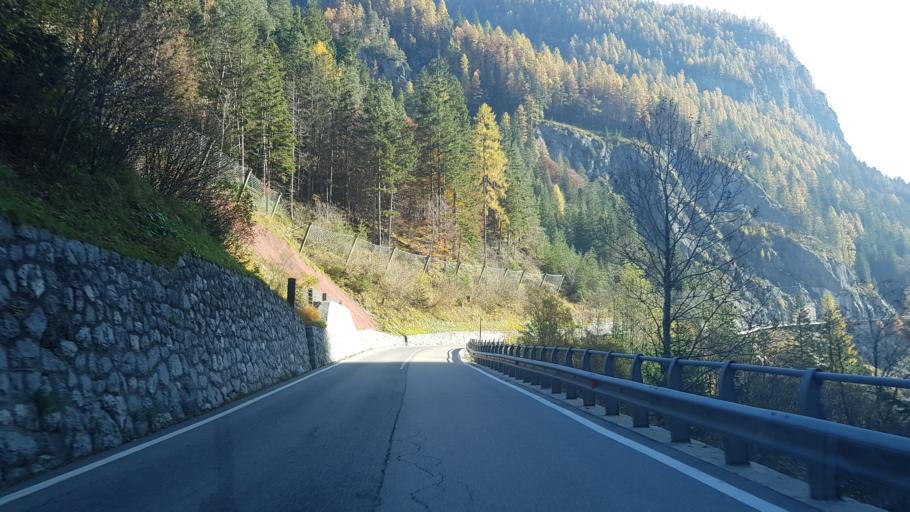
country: IT
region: Veneto
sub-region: Provincia di Belluno
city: Sappada
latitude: 46.5774
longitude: 12.6419
